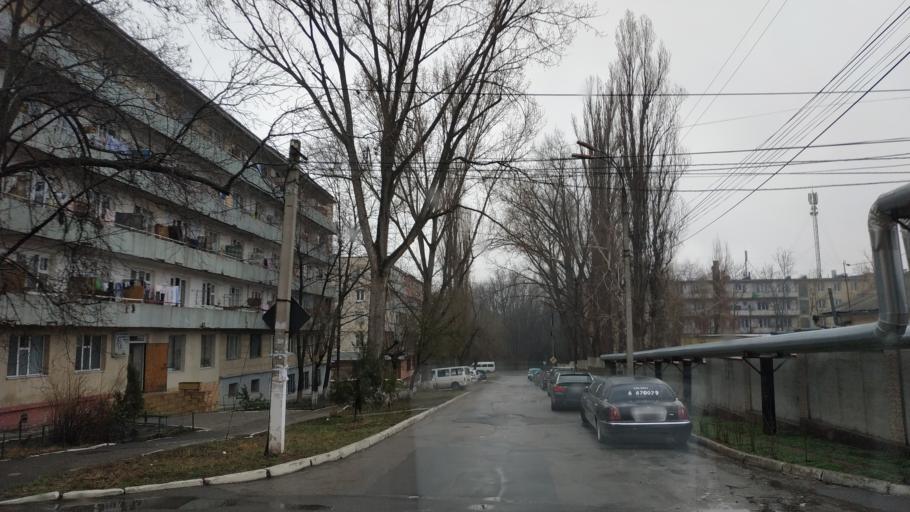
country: MD
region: Chisinau
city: Vatra
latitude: 47.0365
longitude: 28.7822
